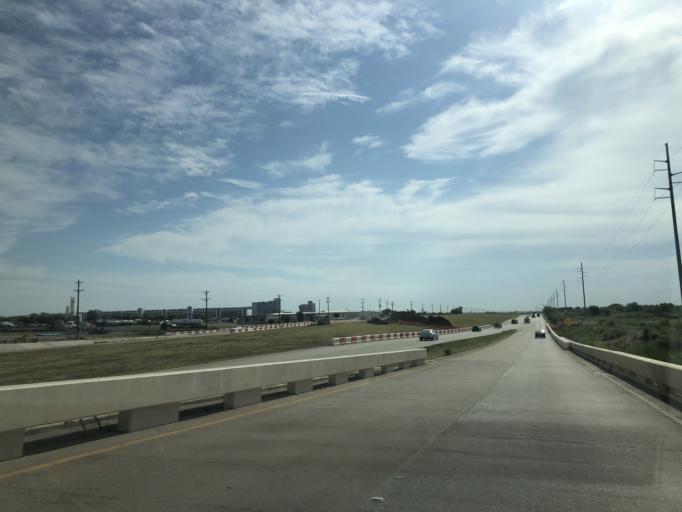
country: US
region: Texas
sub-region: Denton County
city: Justin
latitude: 33.0263
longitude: -97.2990
